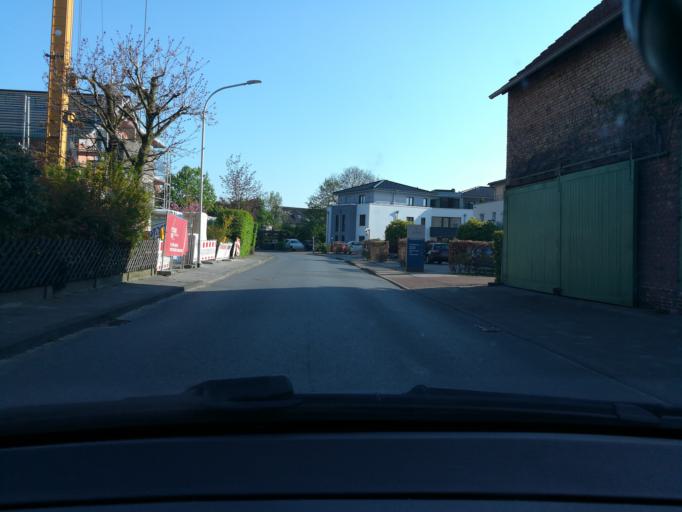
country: DE
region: North Rhine-Westphalia
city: Versmold
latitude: 52.0376
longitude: 8.1599
